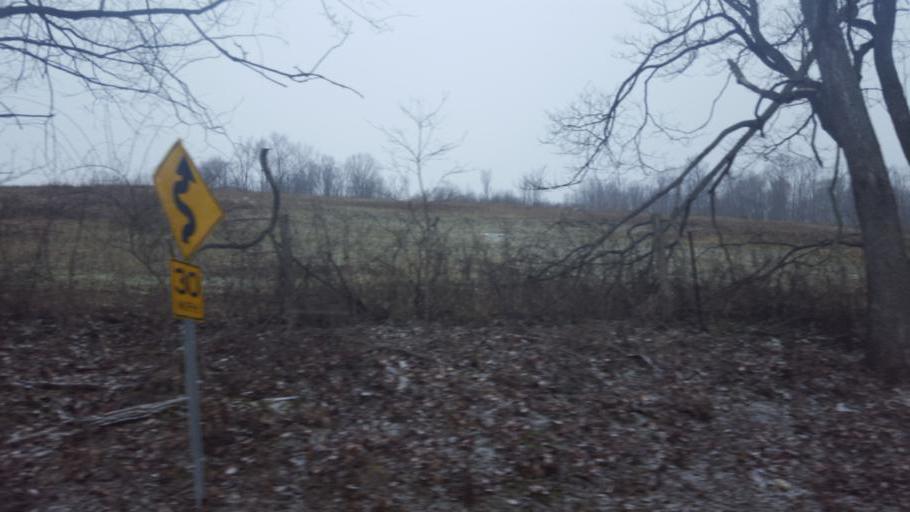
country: US
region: Ohio
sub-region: Coshocton County
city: West Lafayette
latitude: 40.4142
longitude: -81.7733
